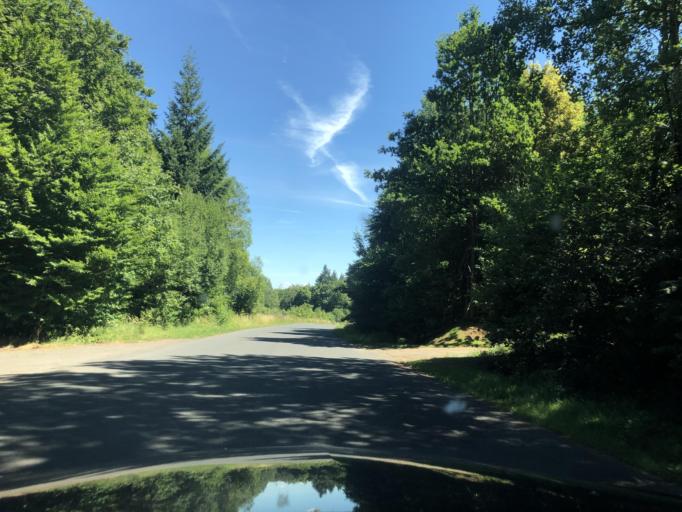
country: DE
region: Hesse
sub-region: Regierungsbezirk Giessen
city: Grebenhain
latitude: 50.4900
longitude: 9.2979
